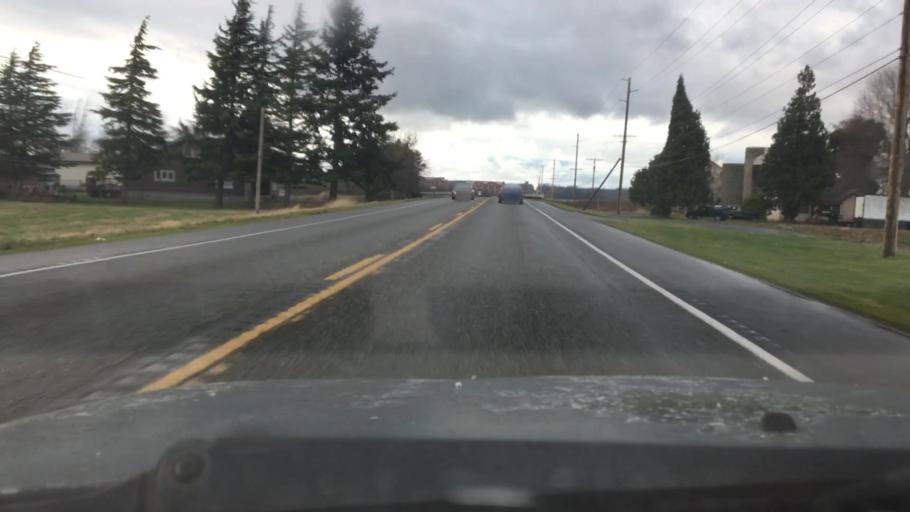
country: US
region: Washington
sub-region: Whatcom County
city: Ferndale
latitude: 48.8192
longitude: -122.6104
